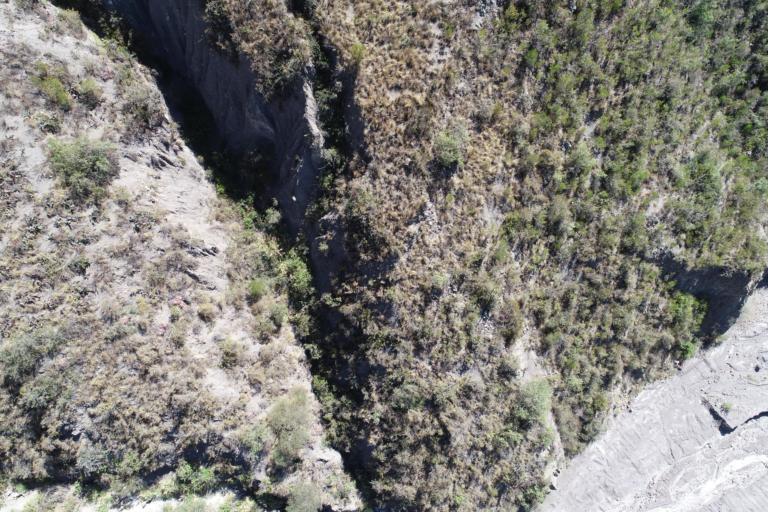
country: BO
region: La Paz
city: La Paz
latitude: -16.6210
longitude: -68.0425
